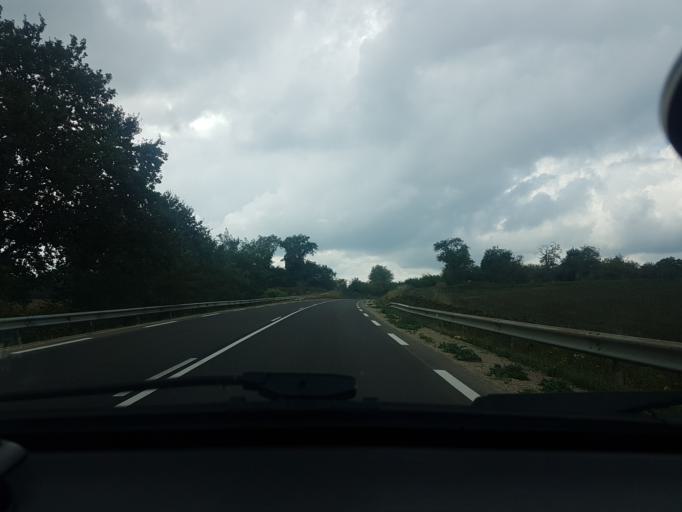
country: FR
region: Franche-Comte
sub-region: Departement de la Haute-Saone
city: Villersexel
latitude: 47.5454
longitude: 6.4649
